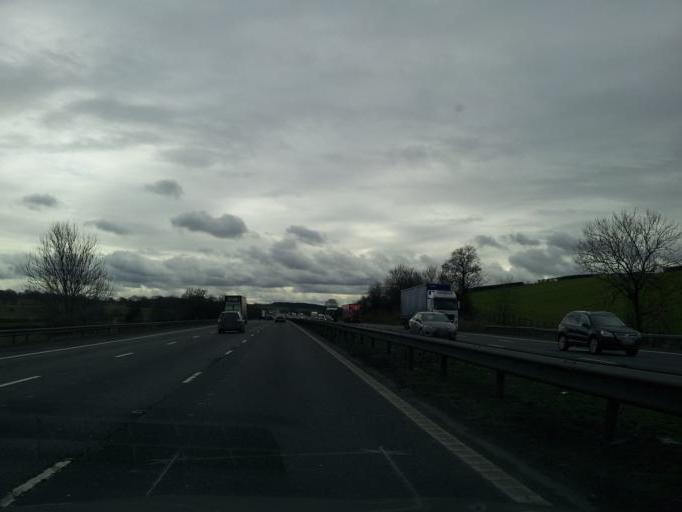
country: GB
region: England
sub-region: Staffordshire
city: Audley
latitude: 53.0431
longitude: -2.3301
